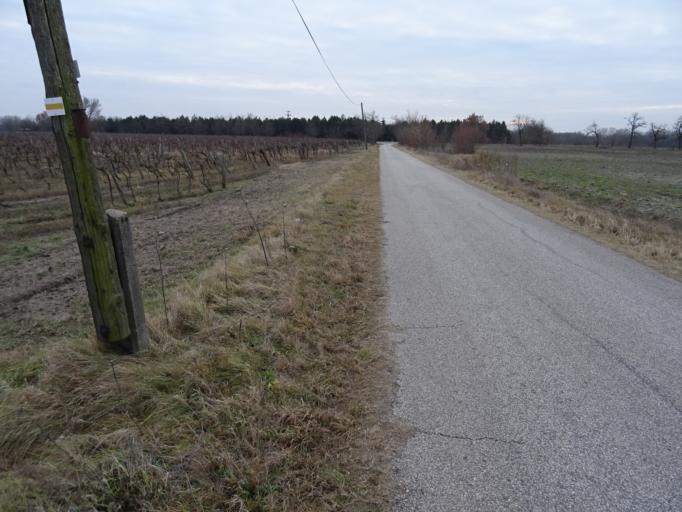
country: HU
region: Bacs-Kiskun
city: Fulopszallas
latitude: 46.8484
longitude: 19.2926
